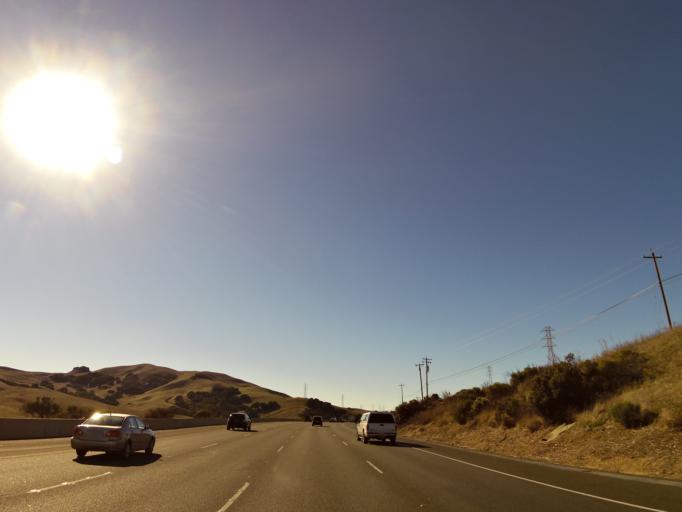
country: US
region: California
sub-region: Solano County
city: Green Valley
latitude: 38.1914
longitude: -122.1686
